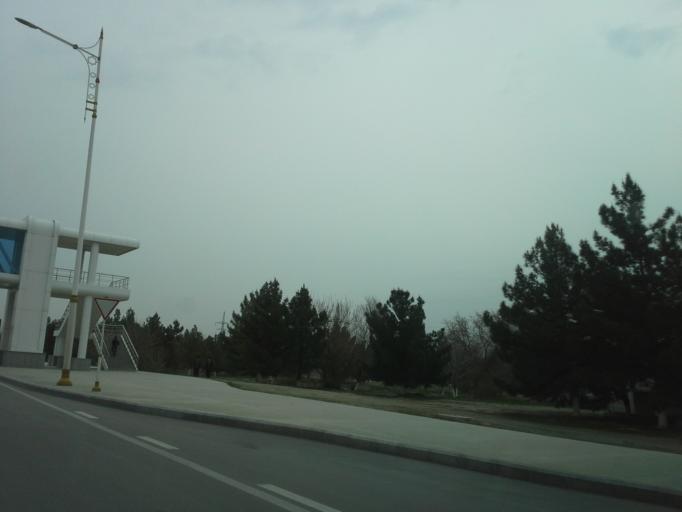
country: TM
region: Ahal
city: Ashgabat
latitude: 37.9656
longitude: 58.3583
